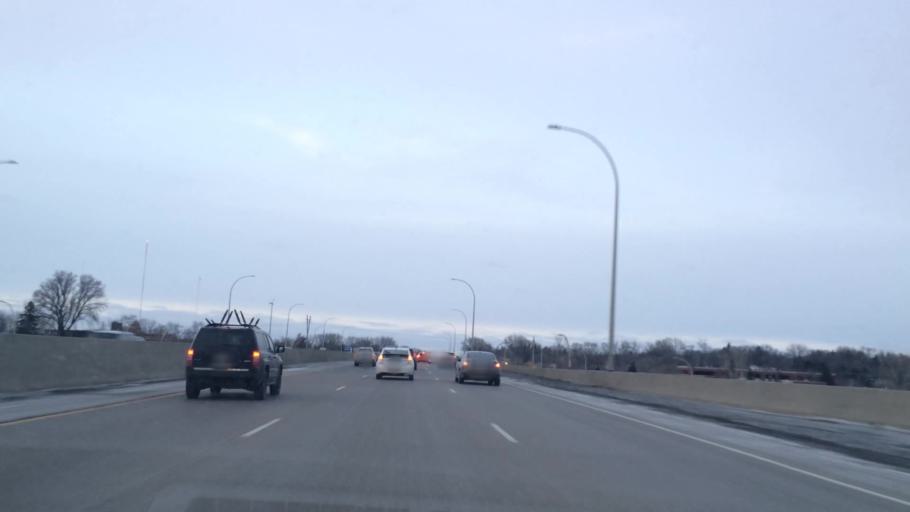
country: US
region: Minnesota
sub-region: Hennepin County
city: Golden Valley
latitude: 44.9837
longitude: -93.3489
